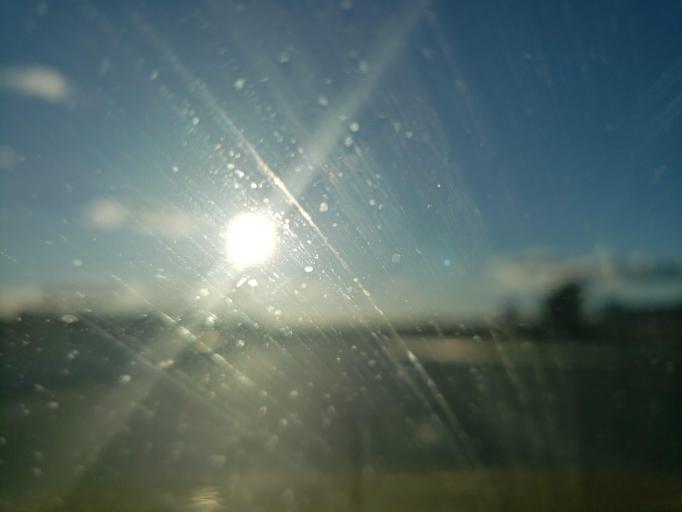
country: ES
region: Castille-La Mancha
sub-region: Province of Toledo
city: Burguillos de Toledo
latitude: 39.8135
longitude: -3.9959
